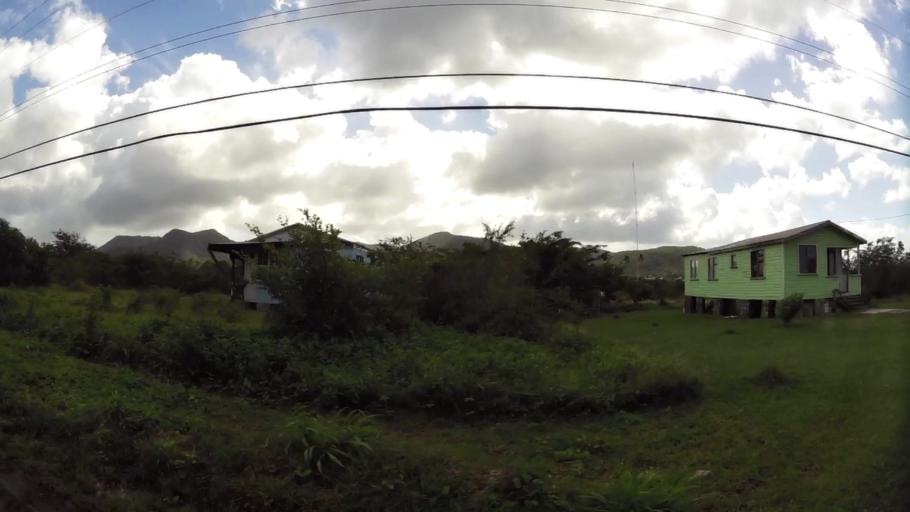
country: AG
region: Saint Mary
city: Bolands
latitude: 17.0784
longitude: -61.8733
